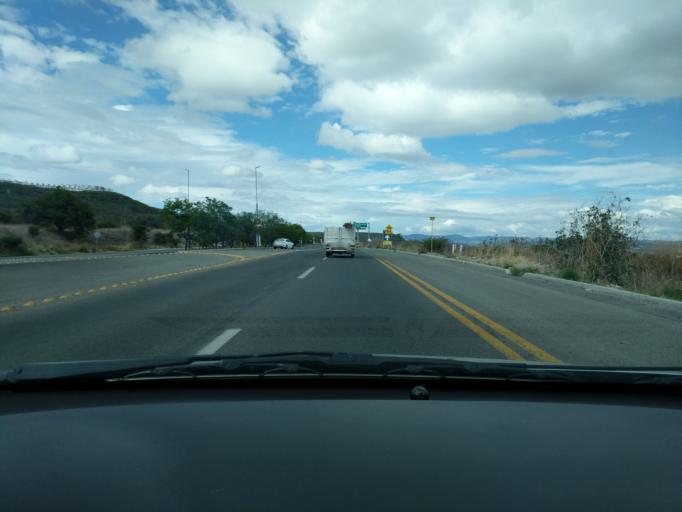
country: MX
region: Queretaro
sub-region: El Marques
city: La Pradera
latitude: 20.6670
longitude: -100.3231
